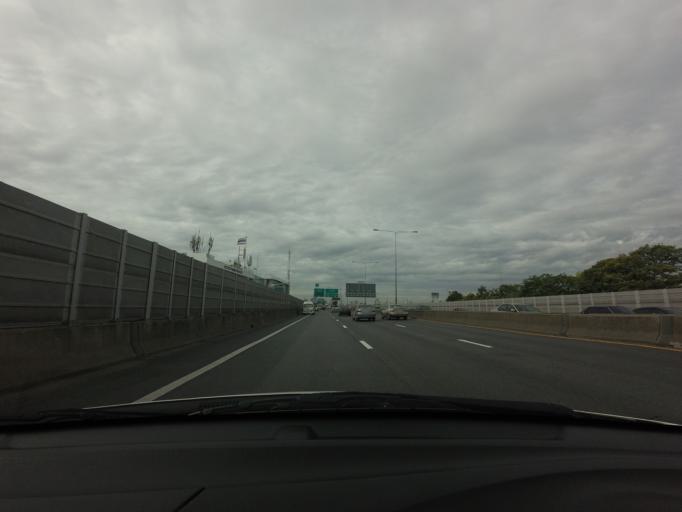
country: TH
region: Bangkok
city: Ratchathewi
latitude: 13.7647
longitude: 100.5269
